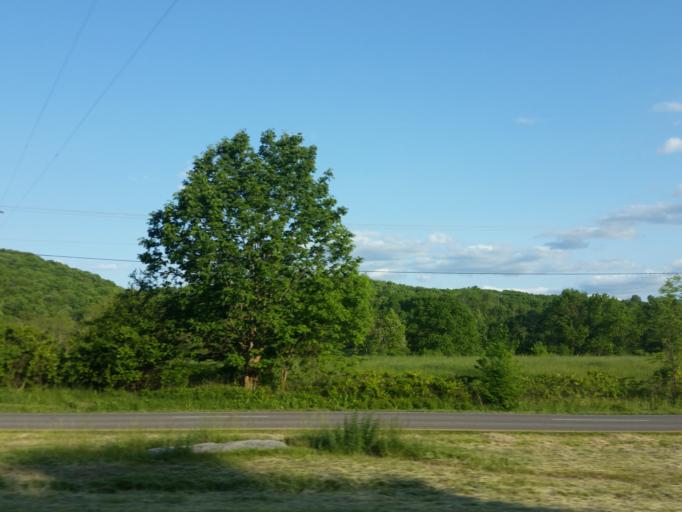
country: US
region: Virginia
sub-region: Russell County
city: Lebanon
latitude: 36.8425
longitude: -82.1354
